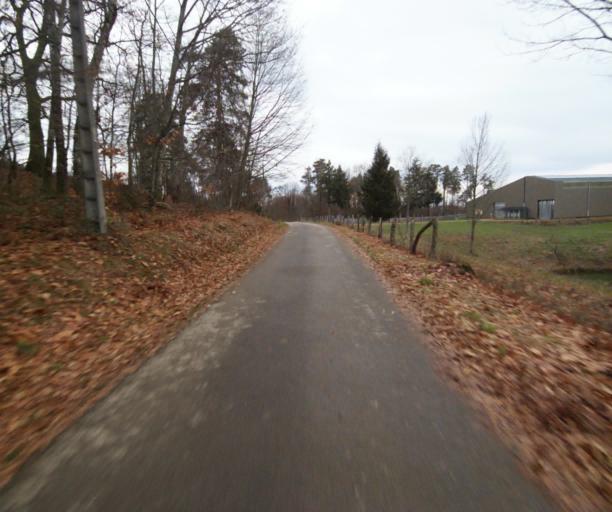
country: FR
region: Limousin
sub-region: Departement de la Correze
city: Cornil
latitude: 45.2330
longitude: 1.6535
